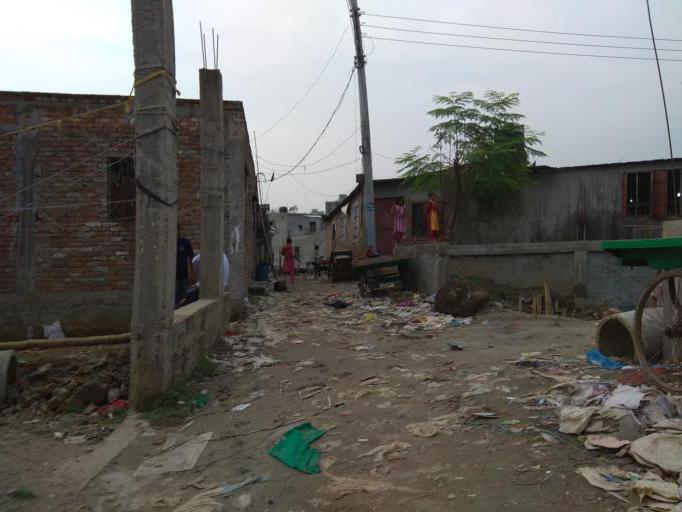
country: BD
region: Dhaka
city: Tungi
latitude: 23.8123
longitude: 90.3798
